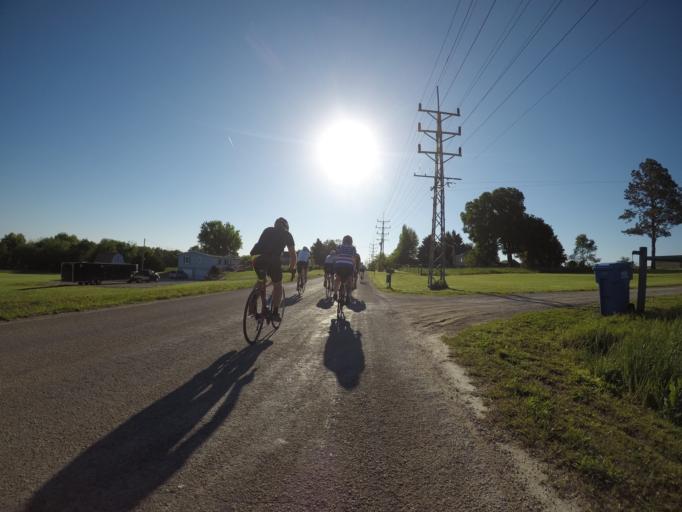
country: US
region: Kansas
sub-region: Shawnee County
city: Topeka
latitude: 39.0516
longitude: -95.5977
